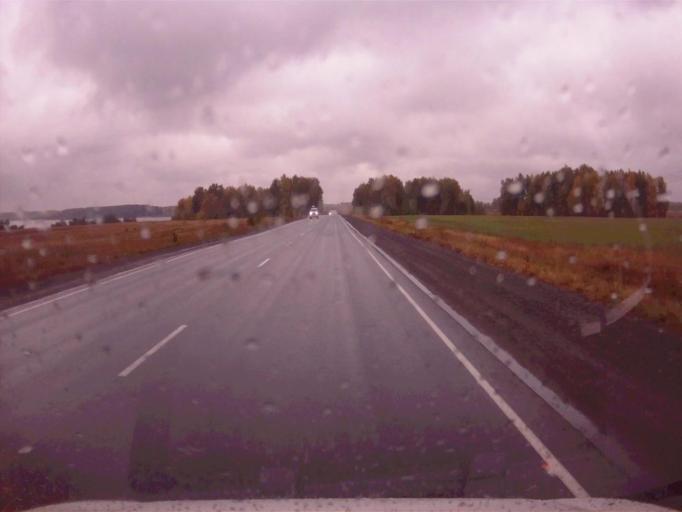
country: RU
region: Chelyabinsk
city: Roshchino
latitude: 55.3854
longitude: 61.1327
